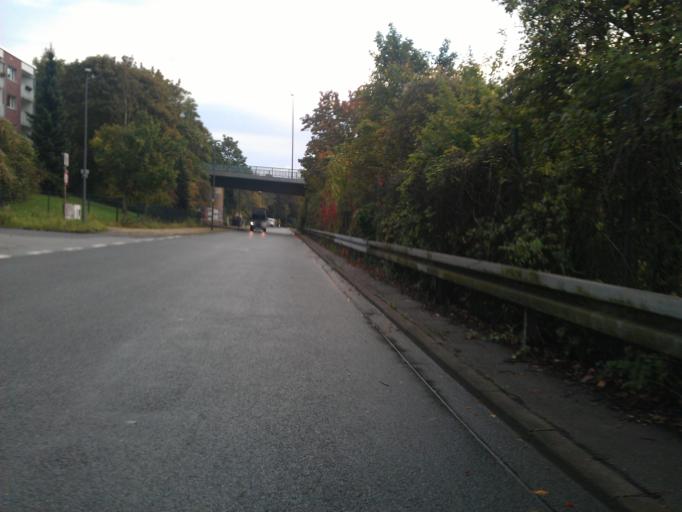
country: DE
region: North Rhine-Westphalia
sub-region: Regierungsbezirk Koln
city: Aachen
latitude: 50.7716
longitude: 6.0569
